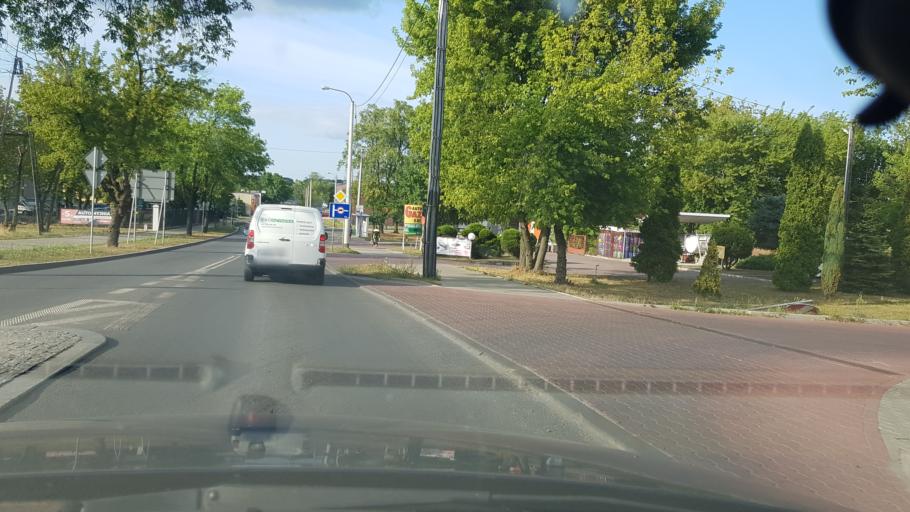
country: PL
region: Lodz Voivodeship
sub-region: Powiat tomaszowski
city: Tomaszow Mazowiecki
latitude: 51.5468
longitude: 20.0146
